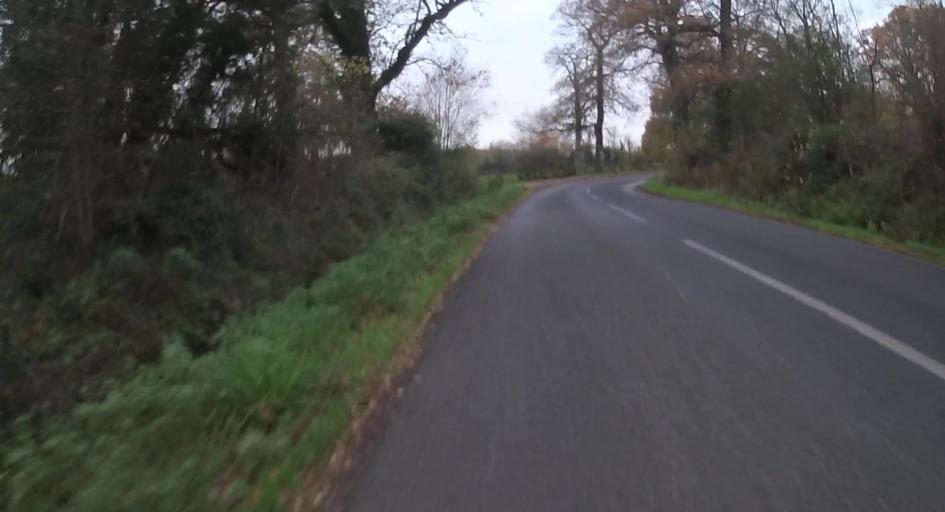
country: GB
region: England
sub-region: Wokingham
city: Swallowfield
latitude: 51.3833
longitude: -0.9365
